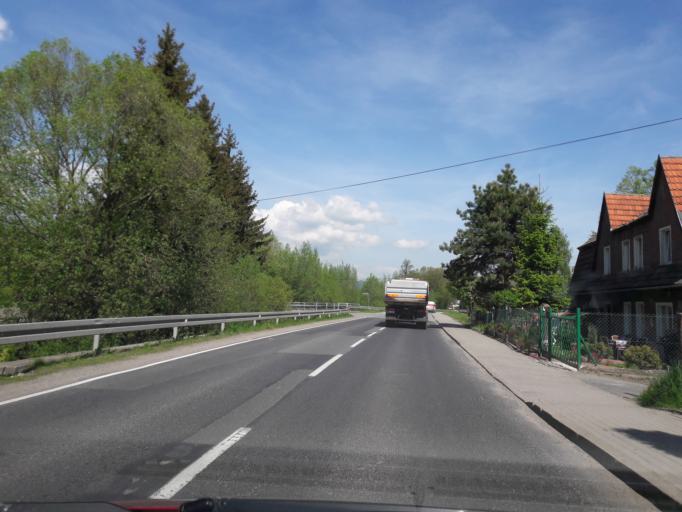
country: PL
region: Lower Silesian Voivodeship
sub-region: Powiat klodzki
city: Bystrzyca Klodzka
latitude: 50.2683
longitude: 16.6596
